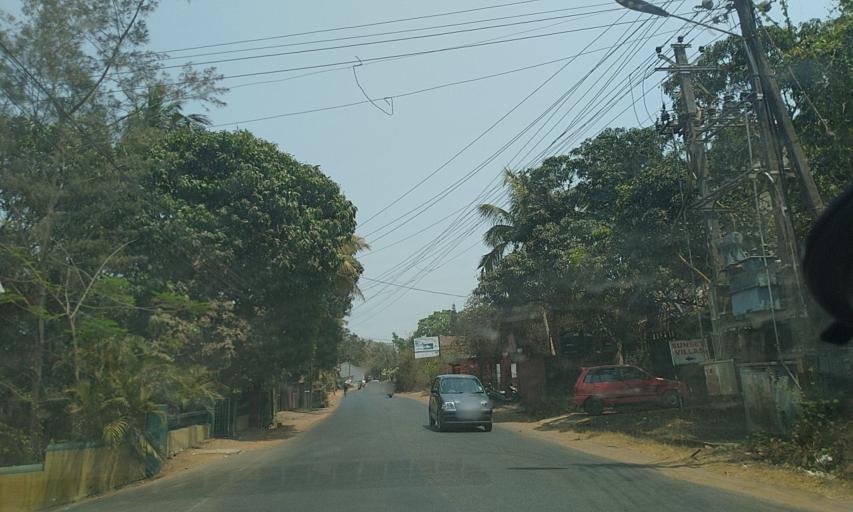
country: IN
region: Goa
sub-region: North Goa
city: Saligao
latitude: 15.5461
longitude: 73.8026
